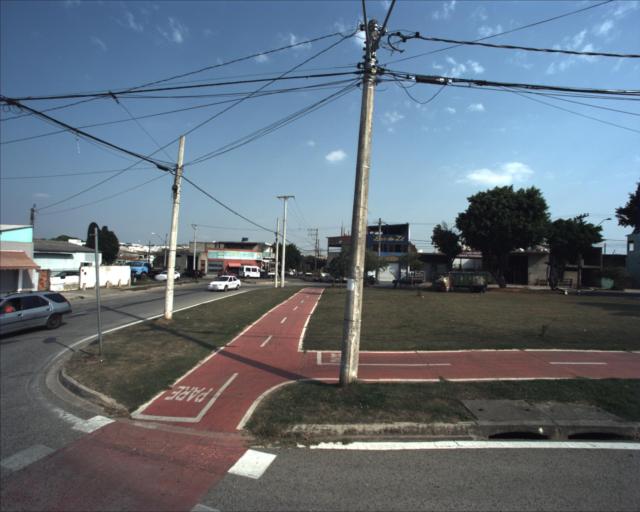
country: BR
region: Sao Paulo
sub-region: Sorocaba
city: Sorocaba
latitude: -23.4332
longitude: -47.4555
